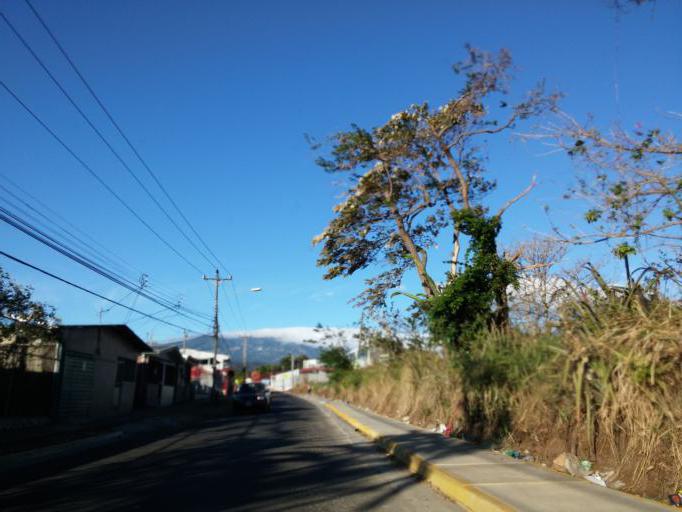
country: CR
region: Alajuela
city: Alajuela
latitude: 10.0096
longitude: -84.2027
